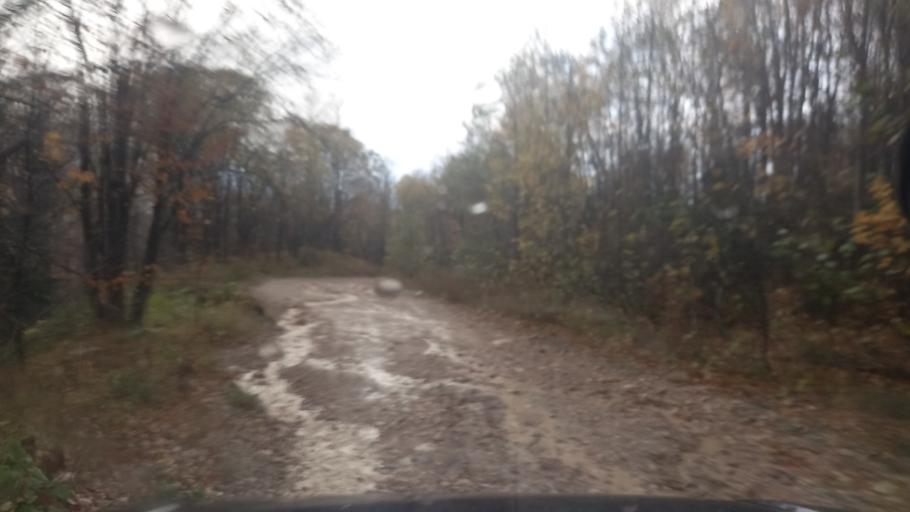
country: RU
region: Krasnodarskiy
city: Gornoye Loo
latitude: 44.0015
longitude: 39.8466
